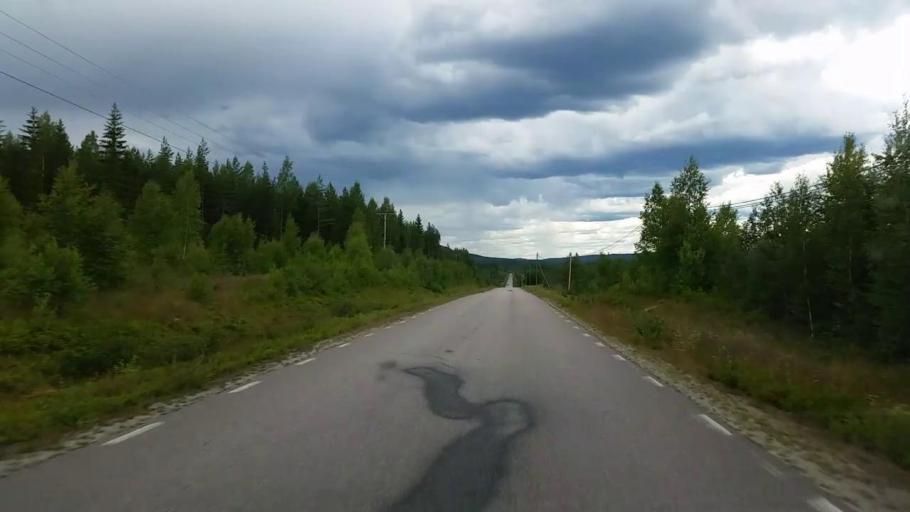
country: SE
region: Gaevleborg
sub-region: Ovanakers Kommun
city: Edsbyn
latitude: 61.4358
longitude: 15.8955
